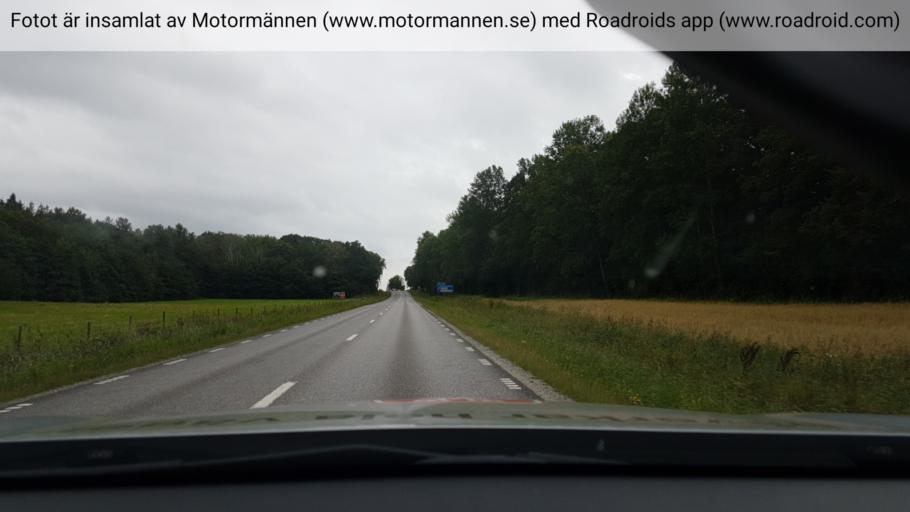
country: SE
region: Vaestra Goetaland
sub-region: Tanums Kommun
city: Grebbestad
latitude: 58.7125
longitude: 11.2633
